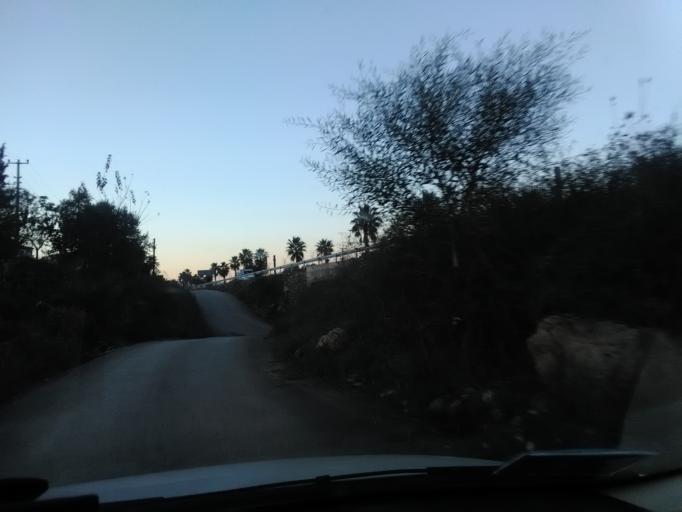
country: TR
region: Antalya
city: Gazipasa
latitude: 36.2491
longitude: 32.3409
